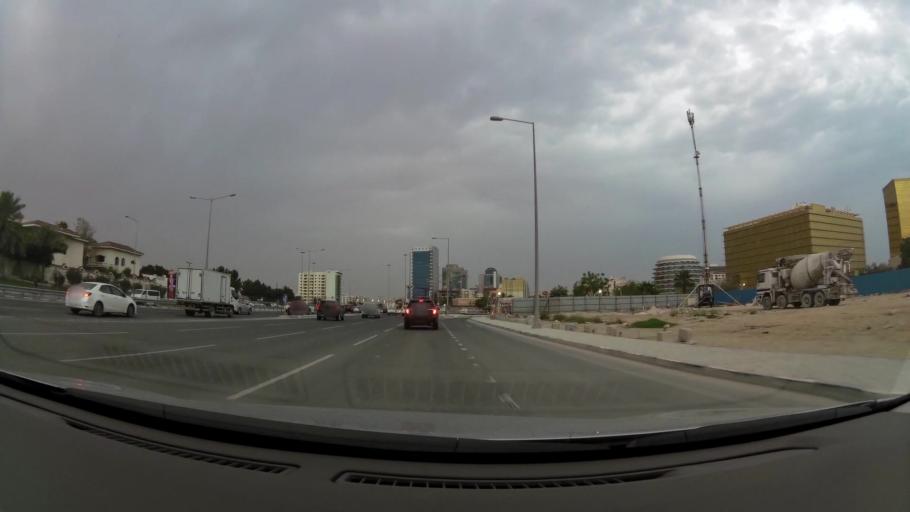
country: QA
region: Baladiyat ad Dawhah
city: Doha
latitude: 25.2707
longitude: 51.5125
